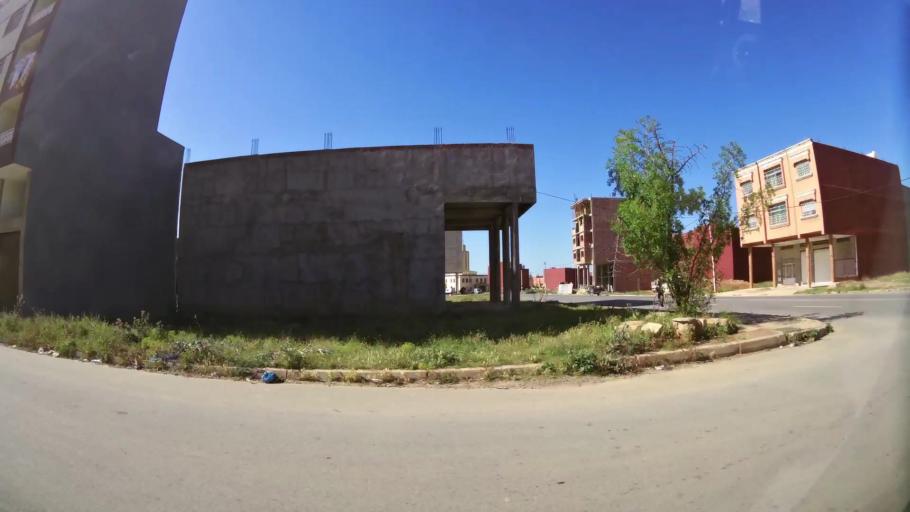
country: MA
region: Oriental
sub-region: Berkane-Taourirt
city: Berkane
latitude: 34.9389
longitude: -2.3347
